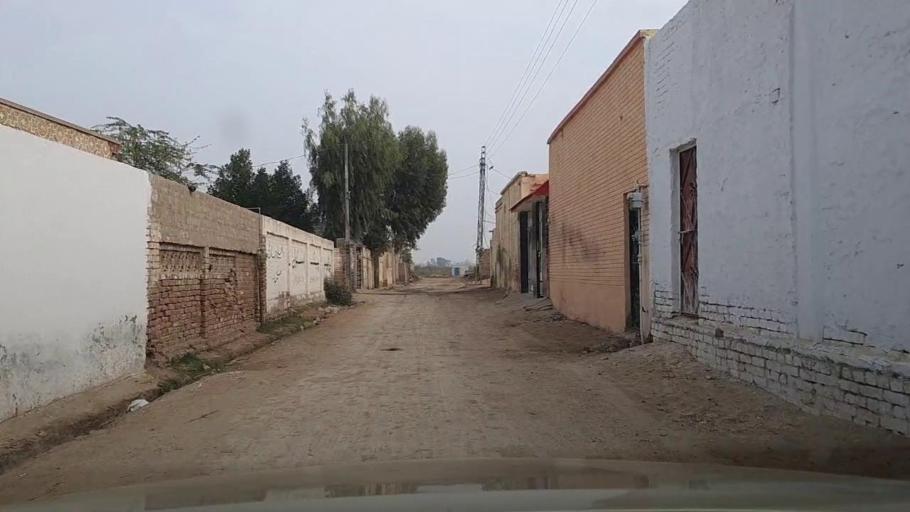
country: PK
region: Sindh
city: Sanghar
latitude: 26.1402
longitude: 68.9664
